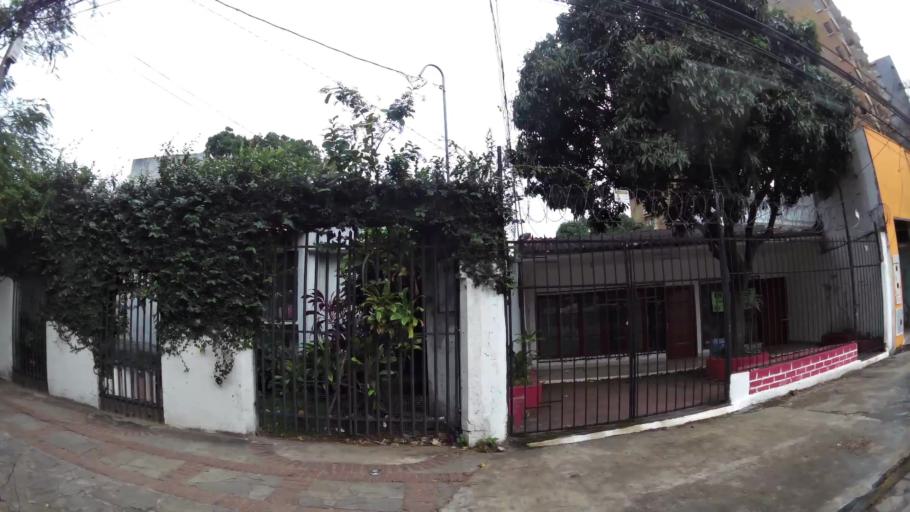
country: BO
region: Santa Cruz
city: Santa Cruz de la Sierra
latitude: -17.7726
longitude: -63.1800
